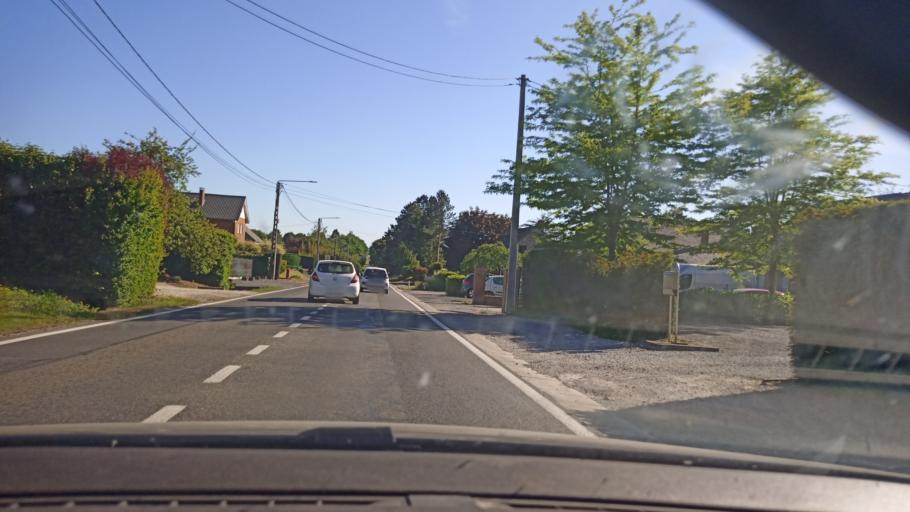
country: BE
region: Wallonia
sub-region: Province du Hainaut
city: Lobbes
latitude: 50.3348
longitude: 4.2653
